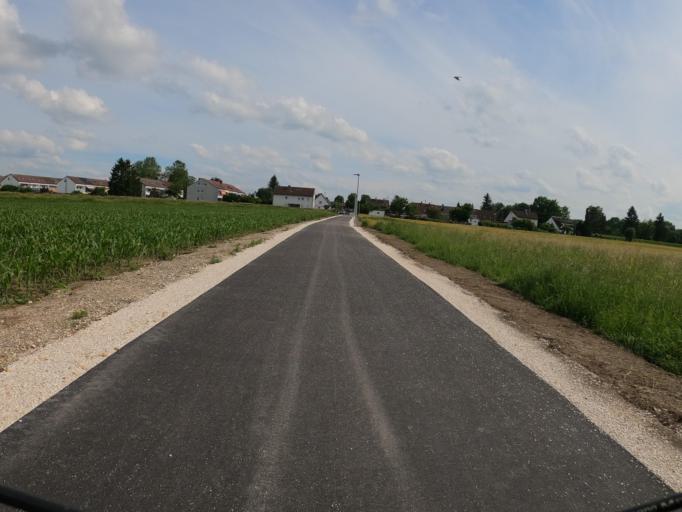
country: DE
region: Bavaria
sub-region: Swabia
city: Neu-Ulm
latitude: 48.3726
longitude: 10.0034
